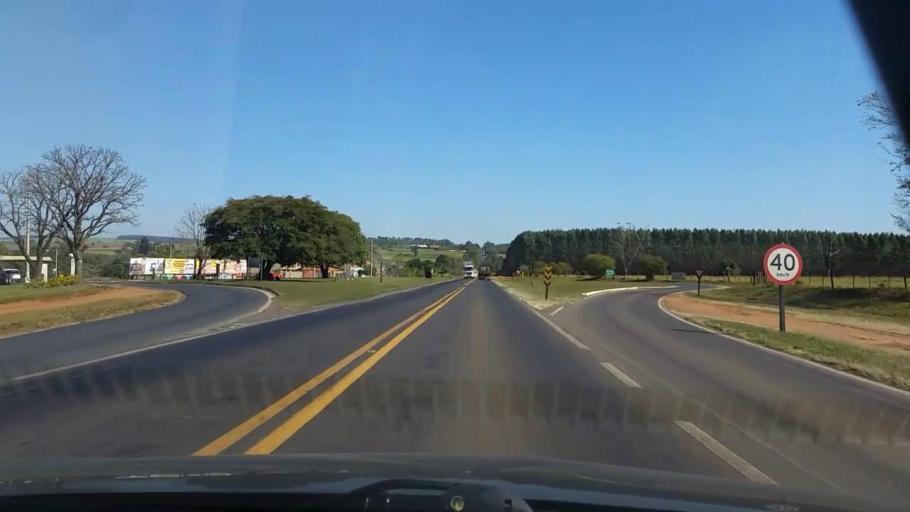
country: BR
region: Sao Paulo
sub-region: Sao Manuel
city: Sao Manuel
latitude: -22.8039
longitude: -48.6688
